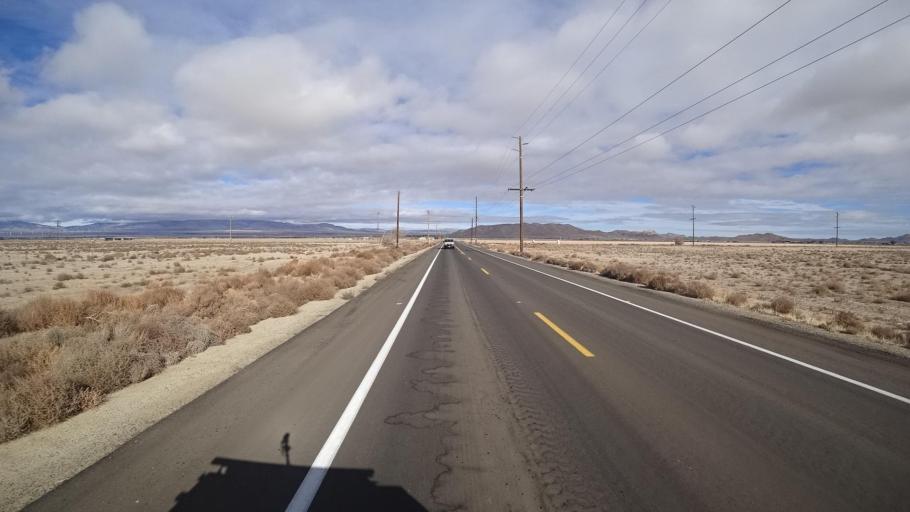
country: US
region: California
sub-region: Kern County
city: Rosamond
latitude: 34.8335
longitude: -118.2907
